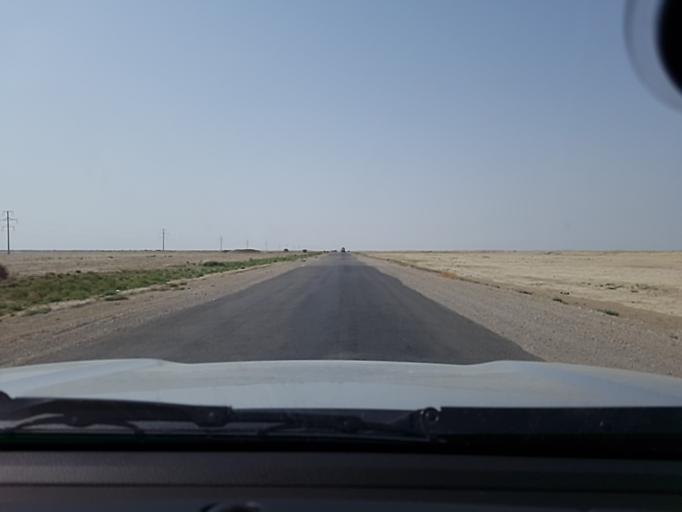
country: TM
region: Balkan
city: Gumdag
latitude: 38.8677
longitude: 54.5943
